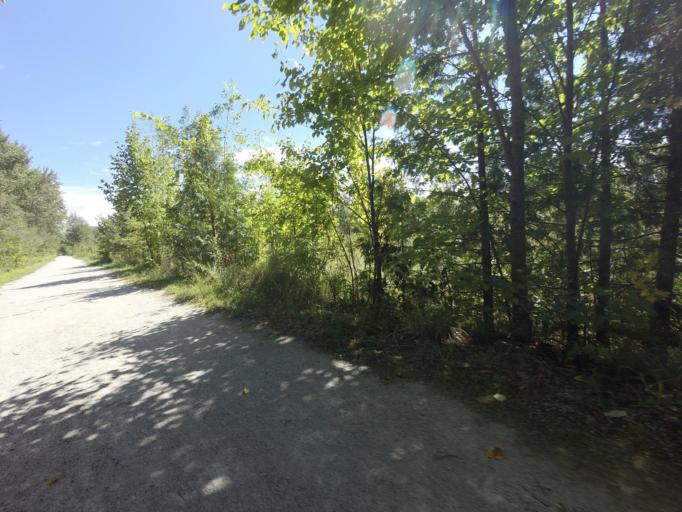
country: CA
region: Ontario
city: Orangeville
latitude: 43.7851
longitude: -80.1478
